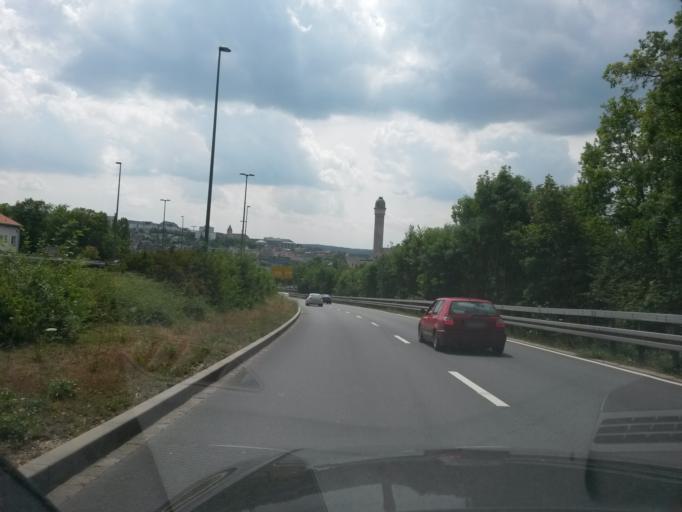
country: DE
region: Bavaria
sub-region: Regierungsbezirk Unterfranken
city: Wuerzburg
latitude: 49.8030
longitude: 9.9627
